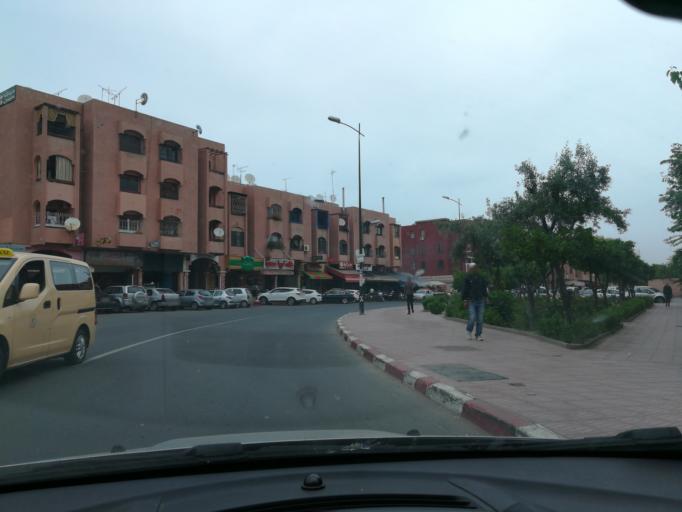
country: MA
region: Marrakech-Tensift-Al Haouz
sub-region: Marrakech
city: Marrakesh
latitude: 31.6577
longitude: -8.0033
